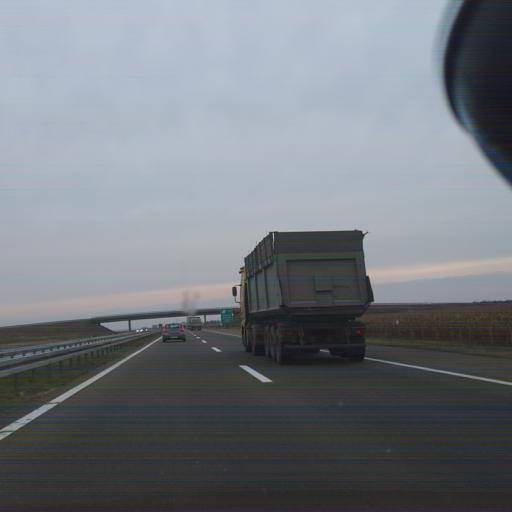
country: RS
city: Novi Karlovci
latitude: 45.0862
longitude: 20.1310
